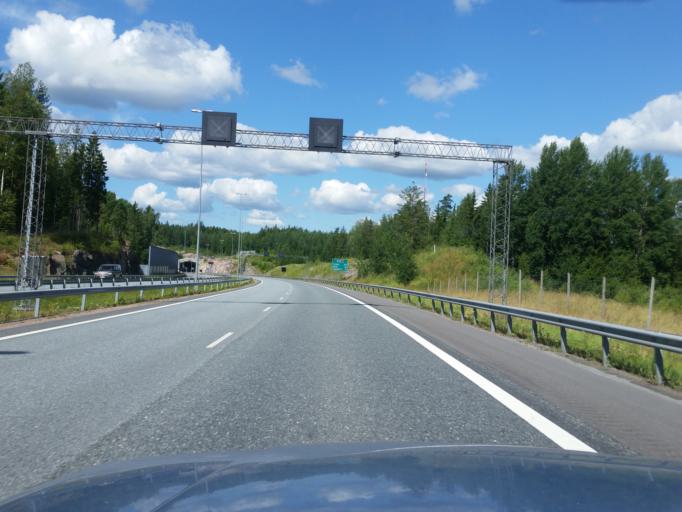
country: FI
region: Uusimaa
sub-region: Helsinki
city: Saukkola
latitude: 60.3219
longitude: 23.9624
